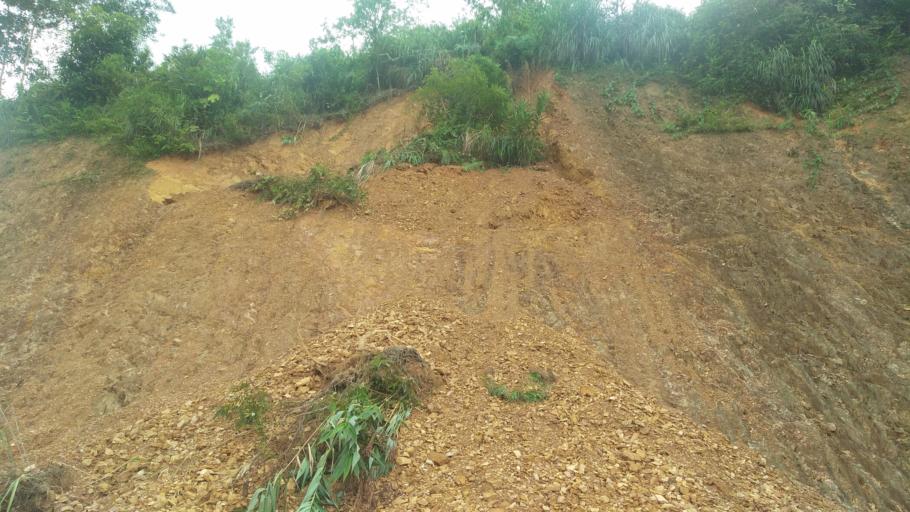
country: VN
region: Ha Giang
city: Thanh Pho Ha Giang
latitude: 22.8571
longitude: 105.0269
